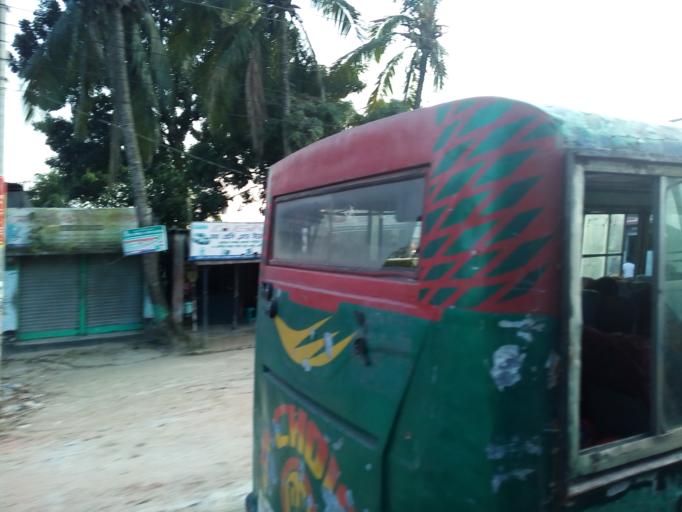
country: BD
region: Dhaka
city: Nagarpur
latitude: 23.8729
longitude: 90.0100
